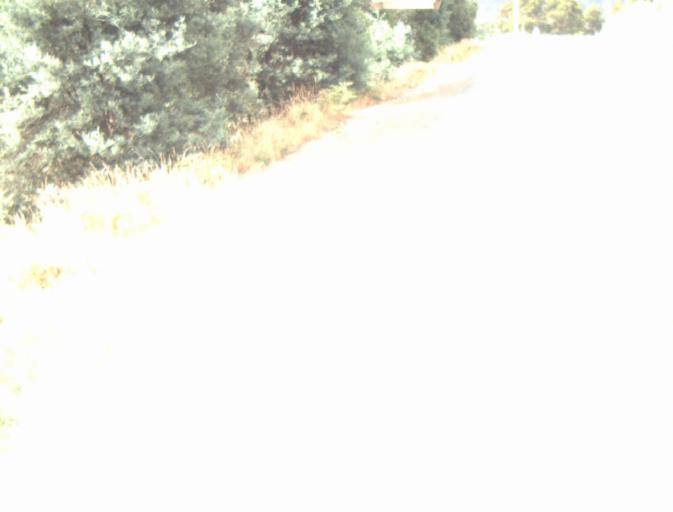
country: AU
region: Tasmania
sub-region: Dorset
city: Scottsdale
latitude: -41.4616
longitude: 147.5953
